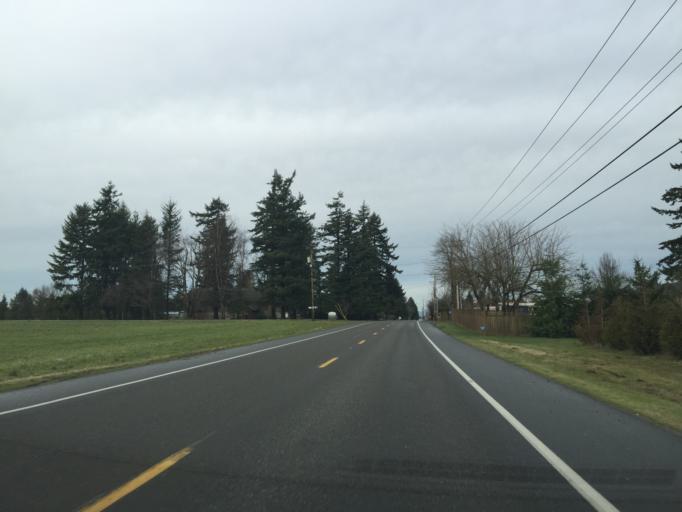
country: US
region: Washington
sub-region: Whatcom County
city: Ferndale
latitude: 48.8826
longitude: -122.5407
